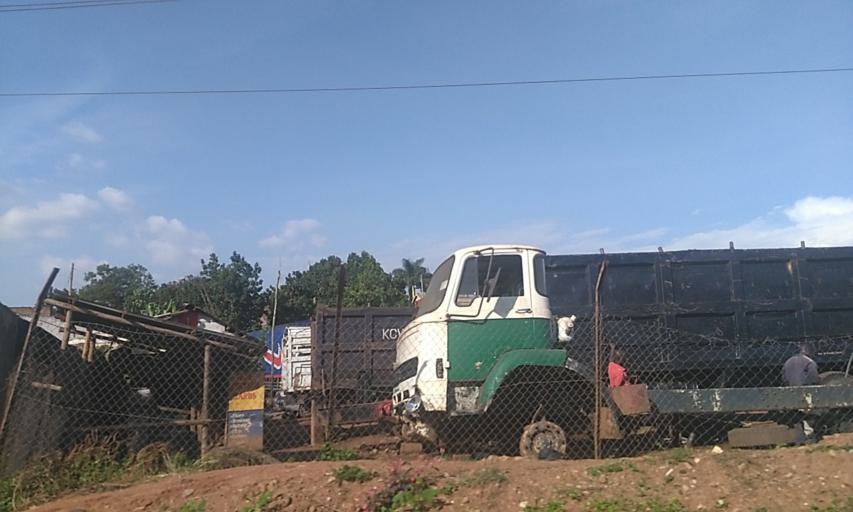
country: UG
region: Central Region
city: Kampala Central Division
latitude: 0.3232
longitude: 32.5421
